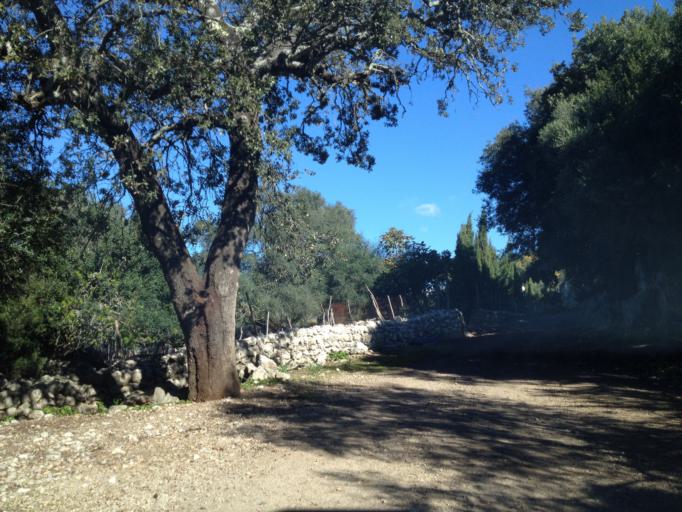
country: ES
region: Balearic Islands
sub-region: Illes Balears
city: Escorca
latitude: 39.8694
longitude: 2.9228
